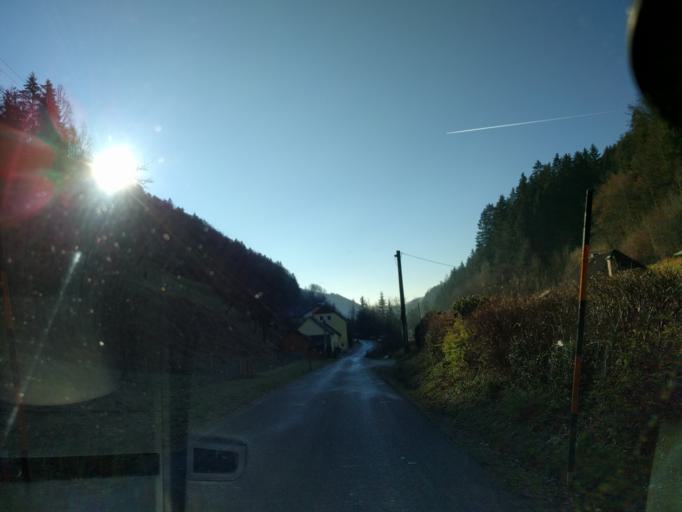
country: AT
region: Upper Austria
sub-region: Politischer Bezirk Urfahr-Umgebung
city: Kirchschlag bei Linz
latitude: 48.3985
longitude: 14.2971
